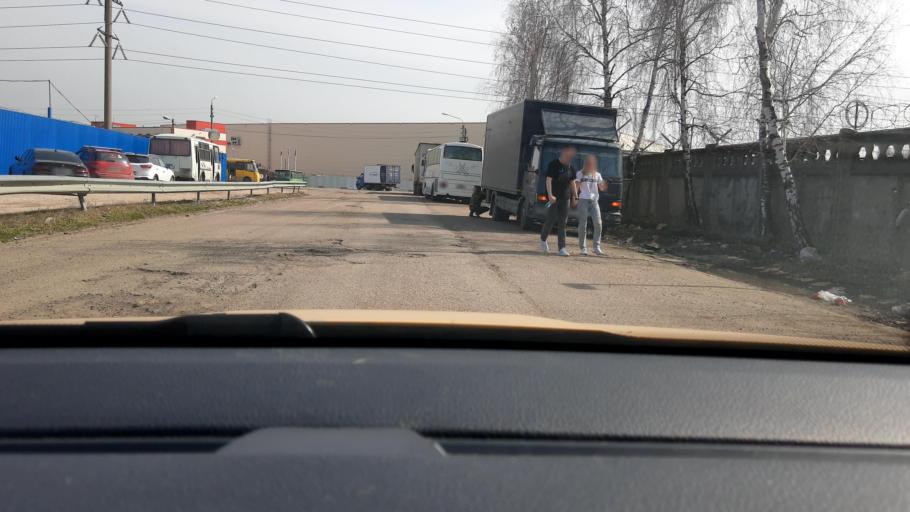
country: RU
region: Moscow
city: Khimki
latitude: 55.9178
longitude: 37.4269
